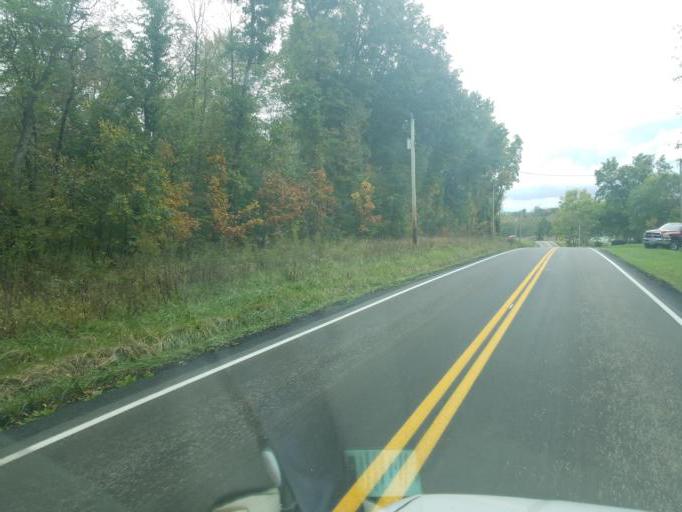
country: US
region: Ohio
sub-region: Wayne County
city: Shreve
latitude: 40.6088
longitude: -82.0606
